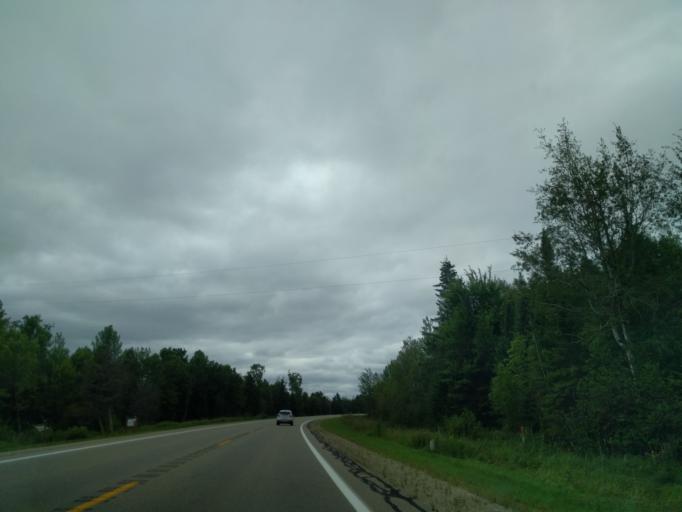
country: US
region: Michigan
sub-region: Delta County
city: Escanaba
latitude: 45.5091
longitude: -87.2877
